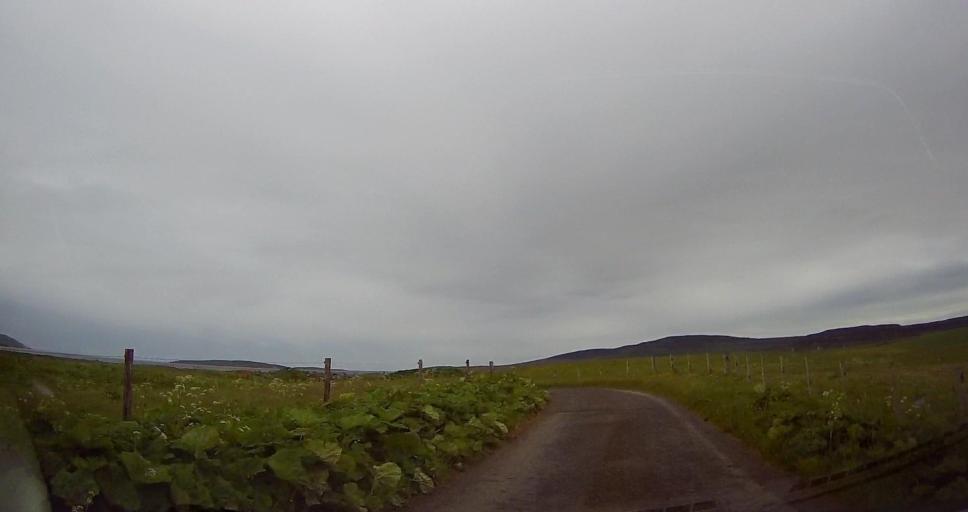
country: GB
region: Scotland
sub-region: Orkney Islands
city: Orkney
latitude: 59.1171
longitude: -3.0845
